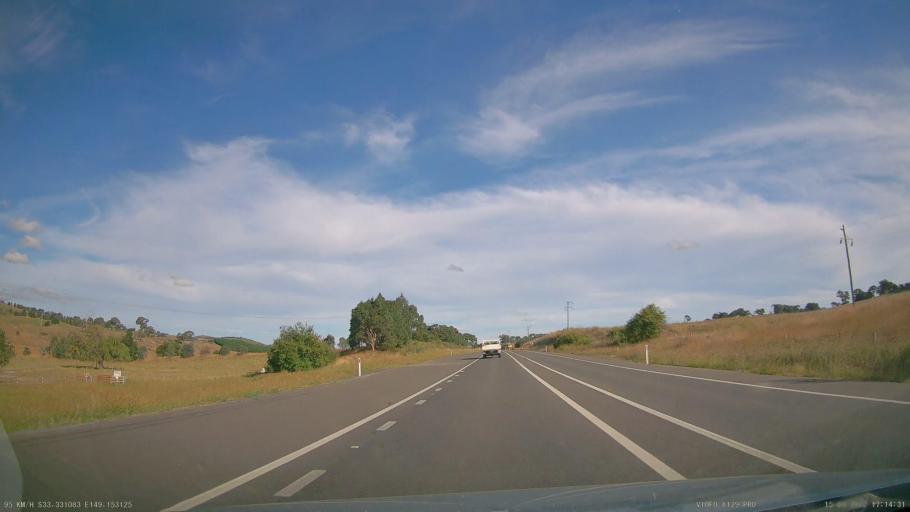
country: AU
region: New South Wales
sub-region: Orange Municipality
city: Orange
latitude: -33.3319
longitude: 149.1532
